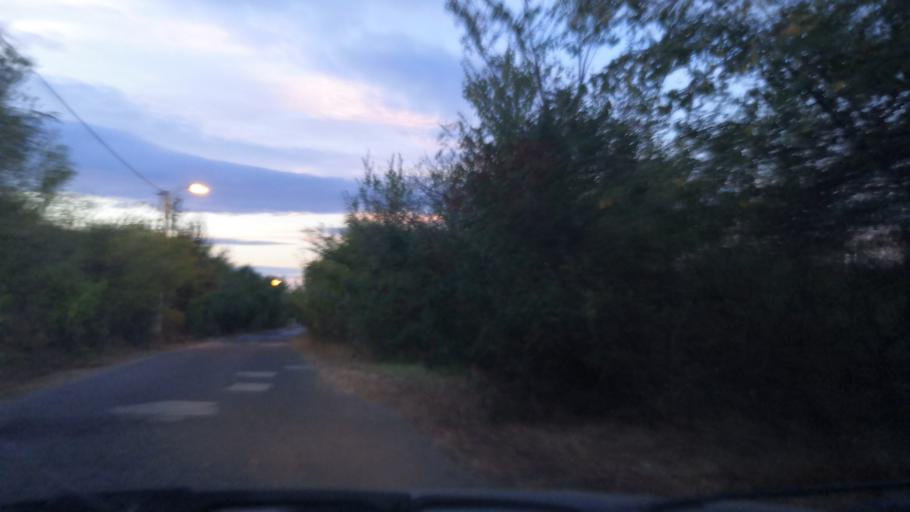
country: RO
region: Mehedinti
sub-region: Comuna Gogosu
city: Balta Verde
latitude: 44.3108
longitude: 22.5485
